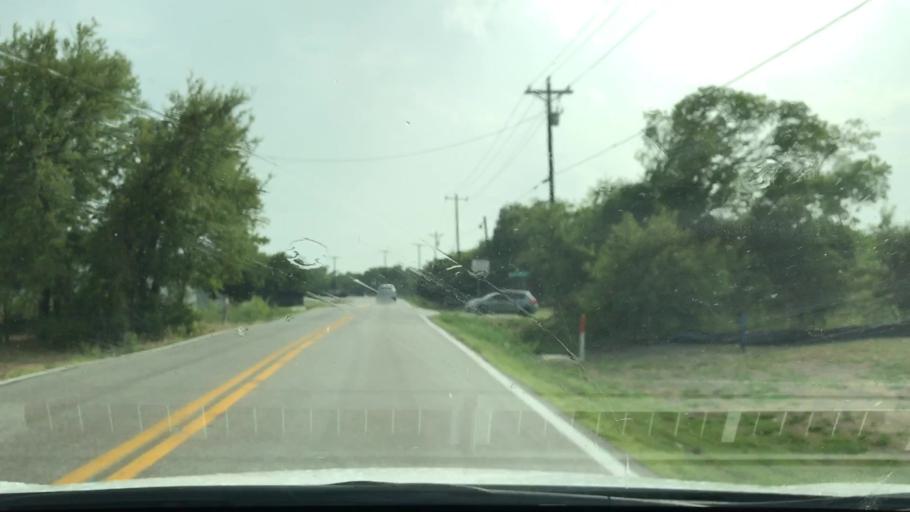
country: US
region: Texas
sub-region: Collin County
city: Wylie
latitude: 32.9810
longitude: -96.5249
